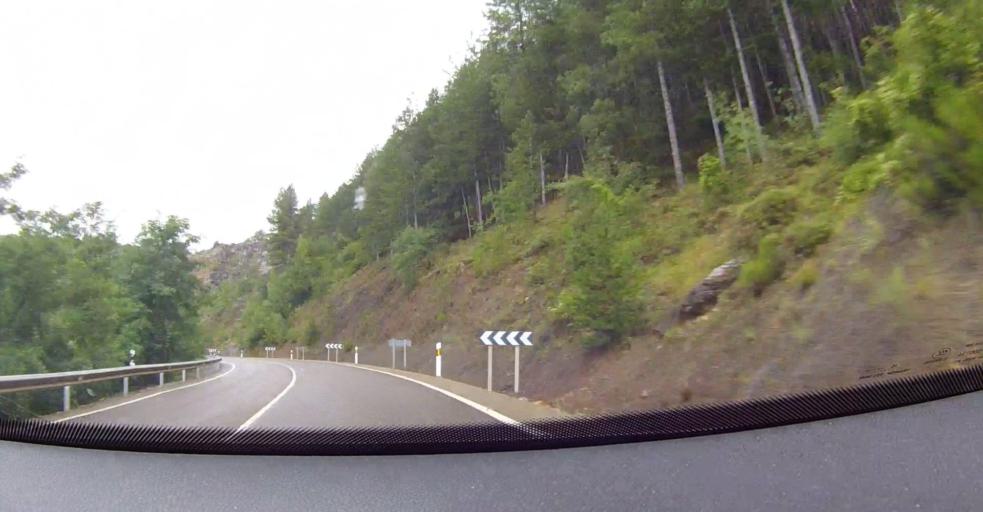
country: ES
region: Castille and Leon
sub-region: Provincia de Leon
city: Cistierna
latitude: 42.8240
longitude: -5.1190
